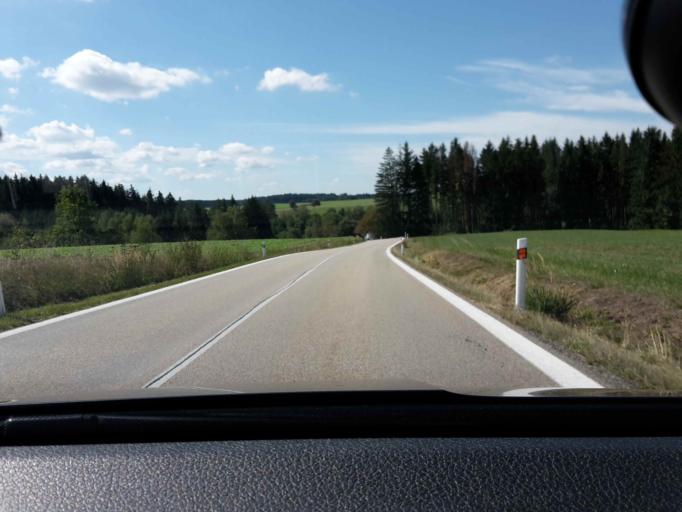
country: CZ
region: Jihocesky
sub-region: Okres Jindrichuv Hradec
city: Studena
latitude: 49.1712
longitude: 15.2570
